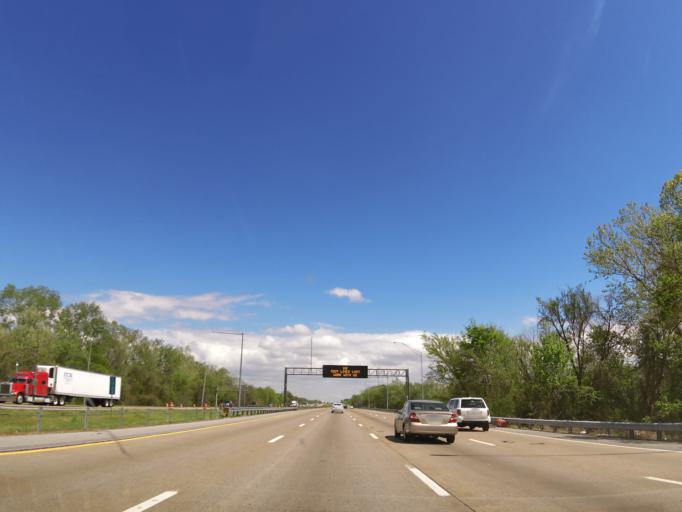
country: US
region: Tennessee
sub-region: Shelby County
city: Memphis
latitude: 35.1921
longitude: -89.9882
